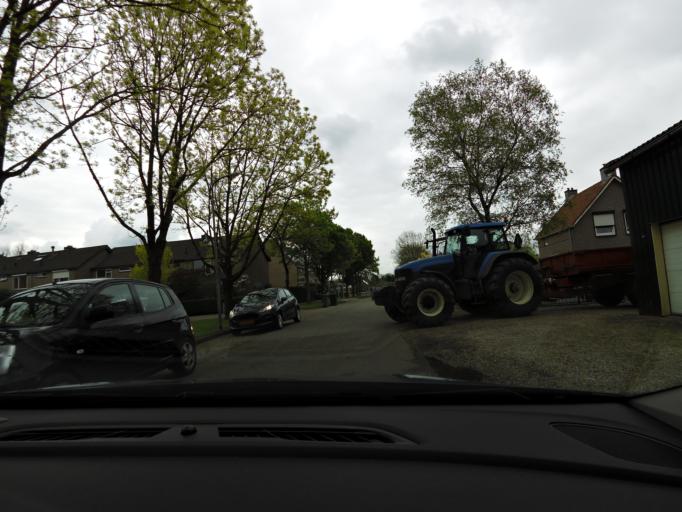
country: NL
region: North Brabant
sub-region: Gemeente Woudrichem
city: Woudrichem
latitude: 51.8565
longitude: 5.0116
